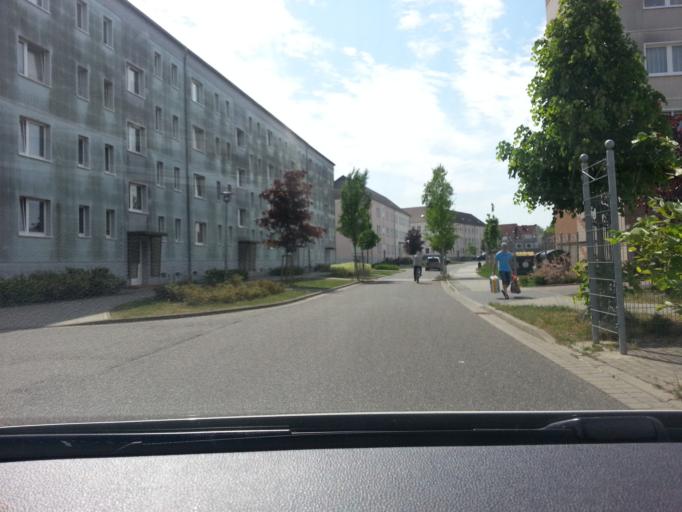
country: DE
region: Mecklenburg-Vorpommern
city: Torgelow
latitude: 53.6354
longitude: 14.0188
